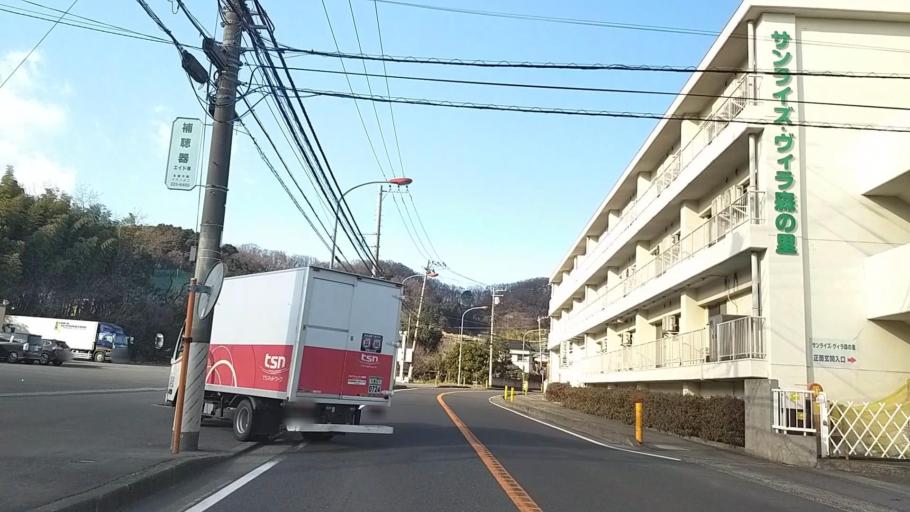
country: JP
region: Kanagawa
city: Atsugi
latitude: 35.4373
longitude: 139.3239
